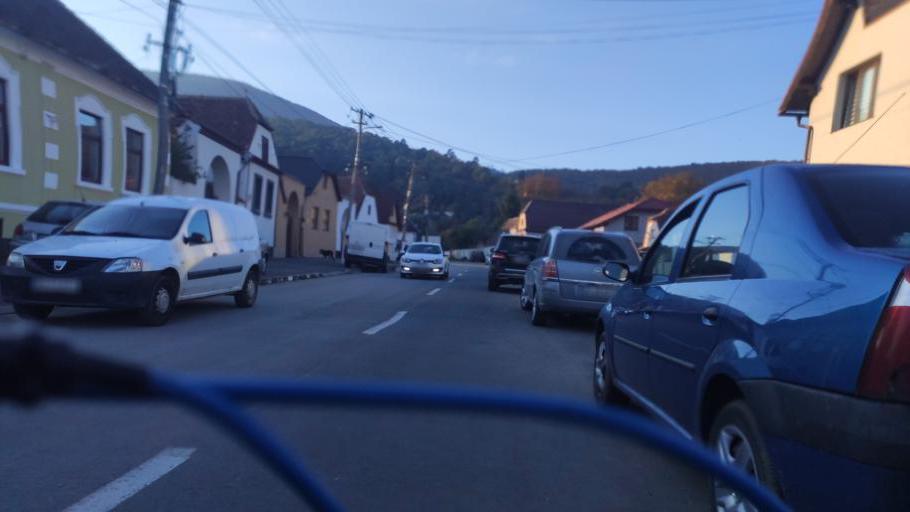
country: RO
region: Brasov
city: Codlea
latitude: 45.6996
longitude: 25.4425
